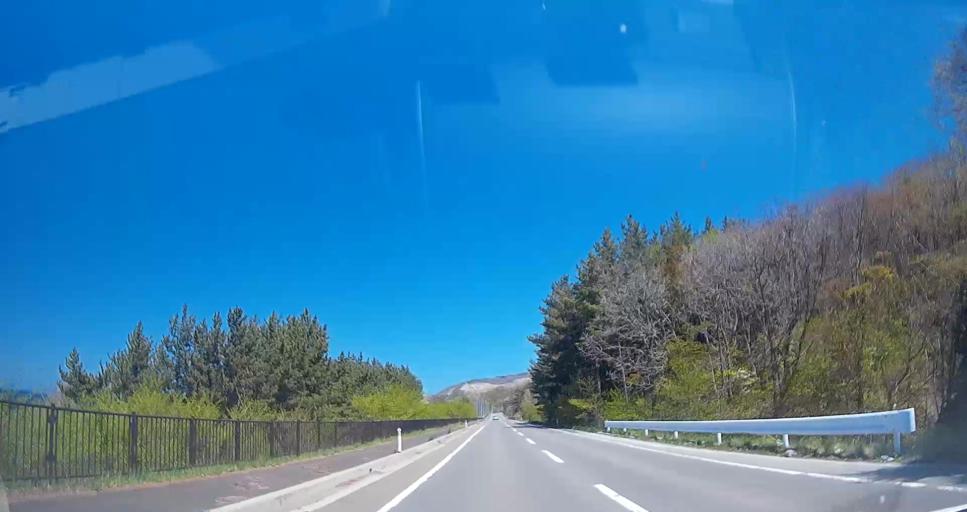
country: JP
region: Aomori
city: Mutsu
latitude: 41.3914
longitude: 141.4148
